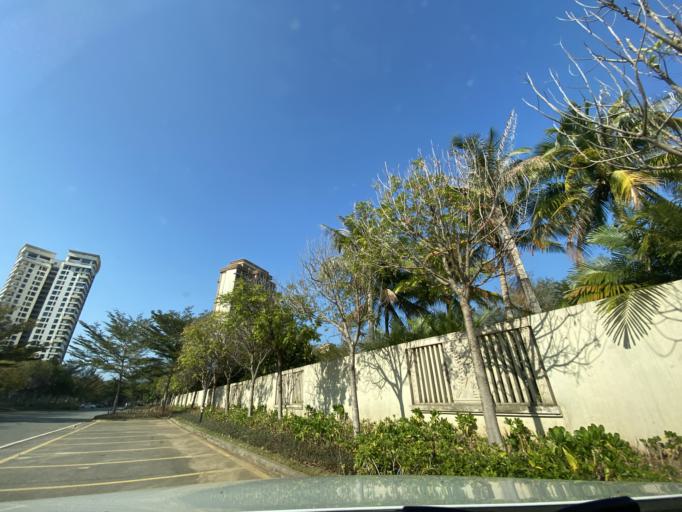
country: CN
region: Hainan
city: Yingzhou
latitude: 18.4145
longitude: 109.8974
